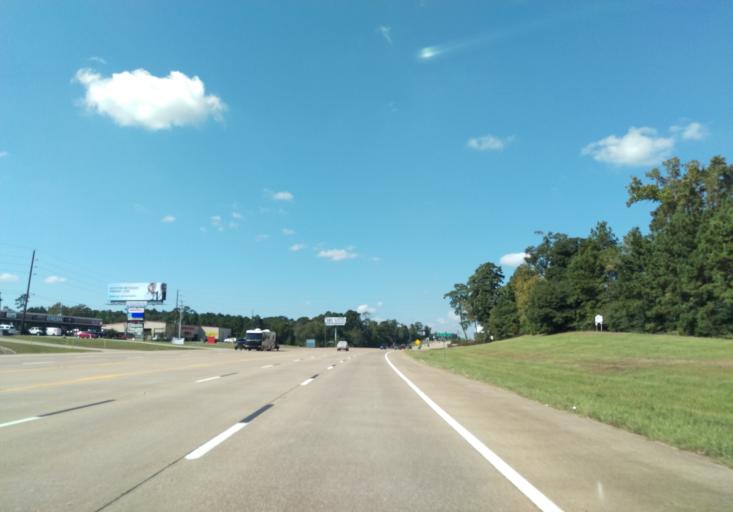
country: US
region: Texas
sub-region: Montgomery County
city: Panorama Village
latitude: 30.3426
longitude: -95.5497
